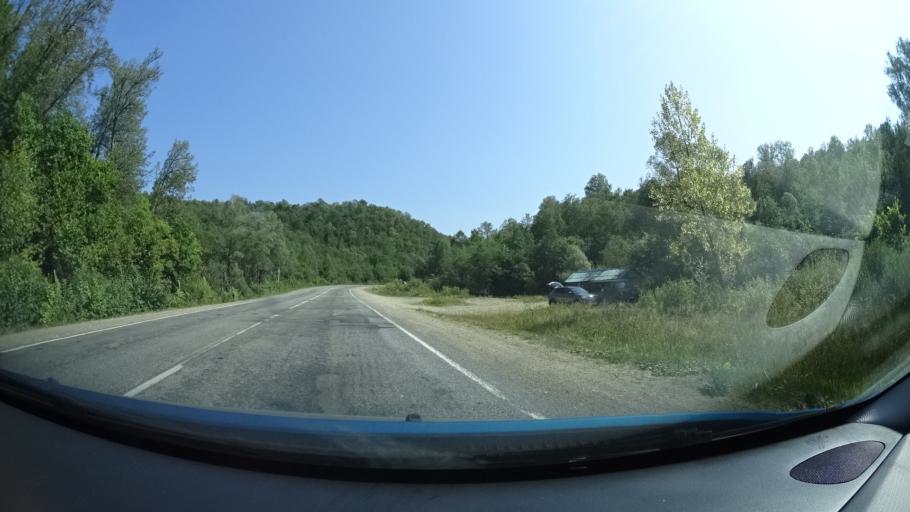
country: RU
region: Bashkortostan
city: Inzer
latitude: 54.3395
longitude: 57.0866
